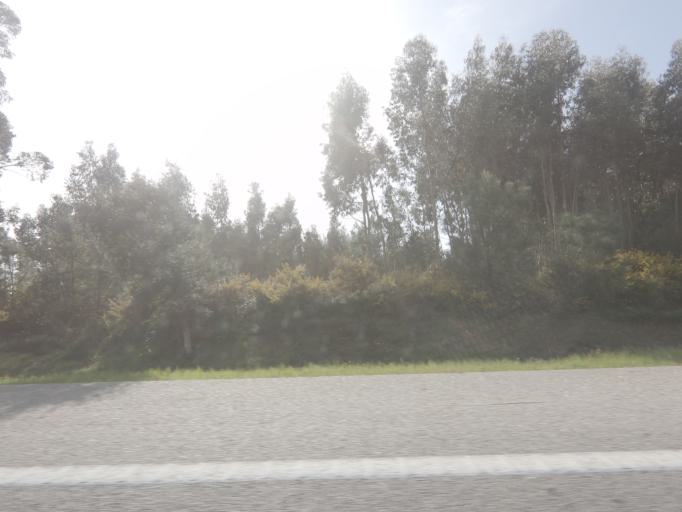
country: PT
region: Aveiro
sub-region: Anadia
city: Sangalhos
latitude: 40.4378
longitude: -8.5116
